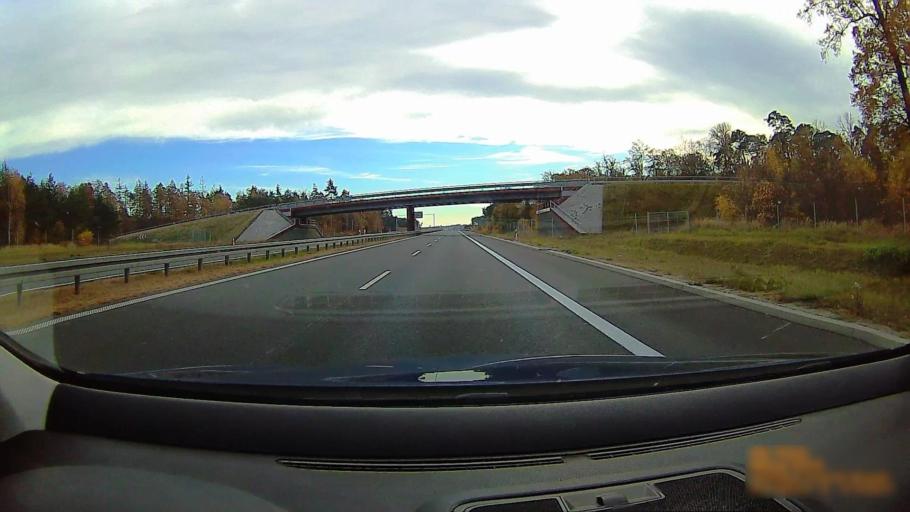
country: PL
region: Greater Poland Voivodeship
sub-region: Powiat ostrowski
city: Ostrow Wielkopolski
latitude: 51.6560
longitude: 17.8650
